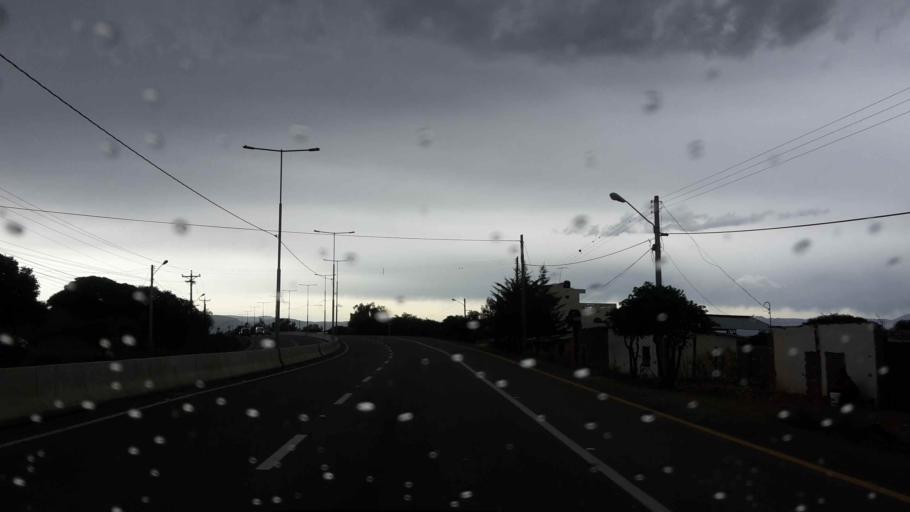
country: BO
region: Cochabamba
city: Tarata
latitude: -17.5470
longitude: -66.0148
